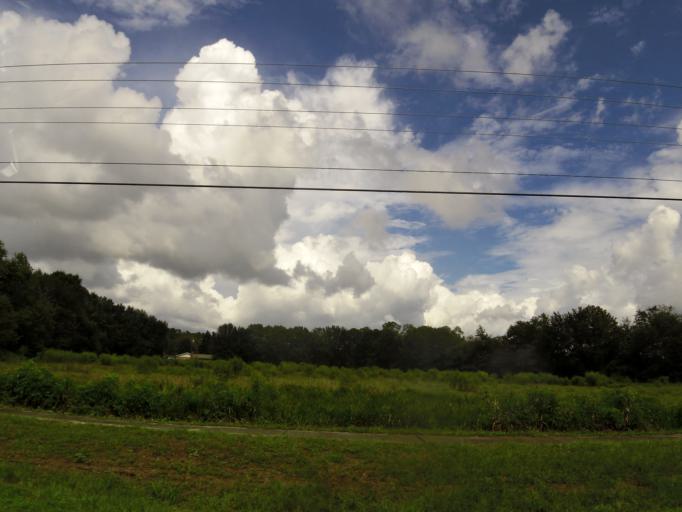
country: US
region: Florida
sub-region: Duval County
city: Baldwin
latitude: 30.1455
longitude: -82.0085
